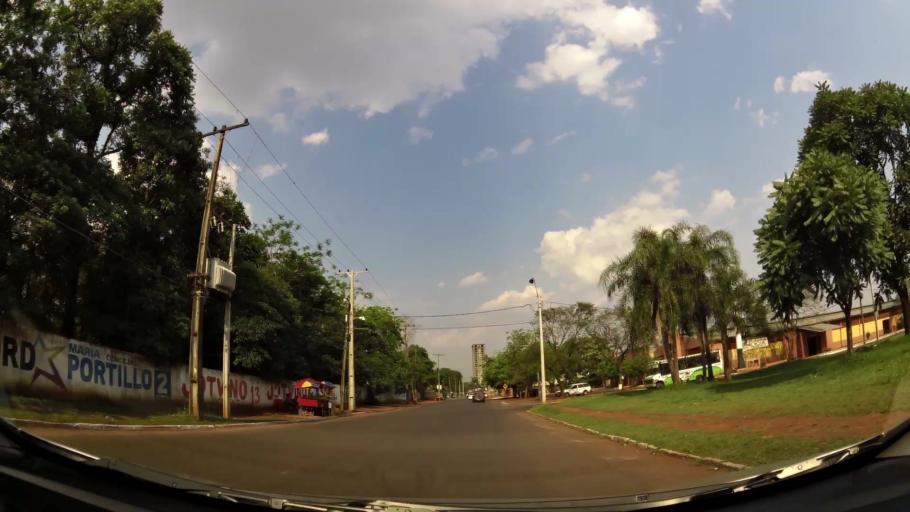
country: PY
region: Alto Parana
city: Presidente Franco
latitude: -25.5252
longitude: -54.6163
